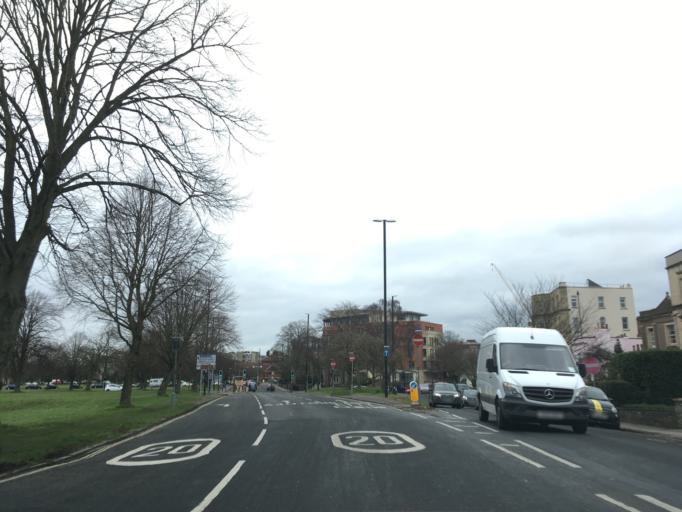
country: GB
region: England
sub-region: Bristol
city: Bristol
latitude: 51.4699
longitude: -2.6175
